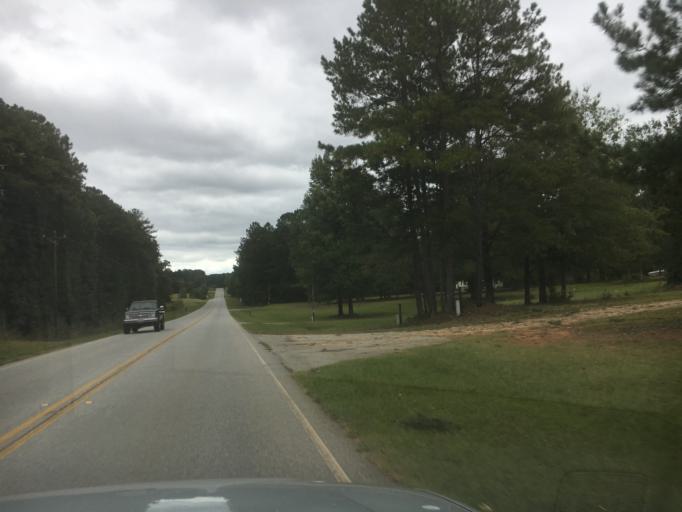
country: US
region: Georgia
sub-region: Lincoln County
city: Lincolnton
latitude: 33.7385
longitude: -82.5495
